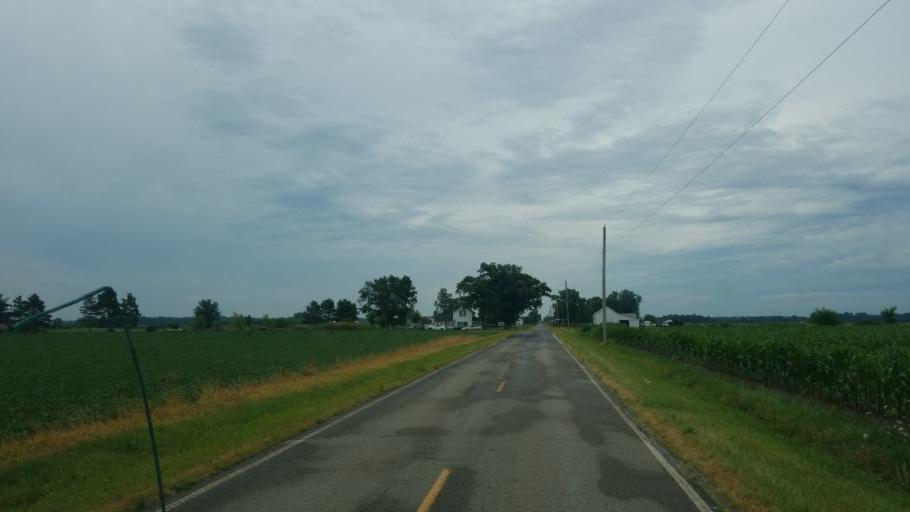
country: US
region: Ohio
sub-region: Defiance County
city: Hicksville
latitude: 41.2790
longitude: -84.6895
